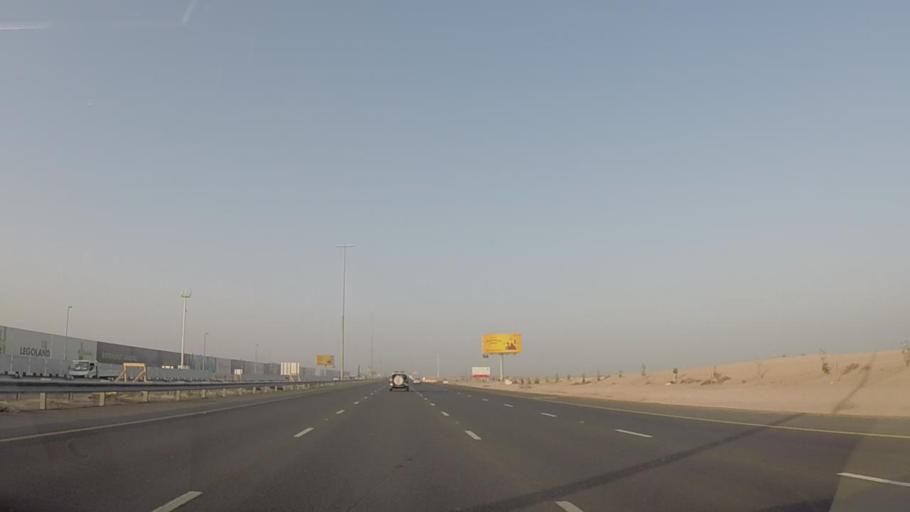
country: AE
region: Dubai
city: Dubai
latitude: 24.9264
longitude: 55.0023
